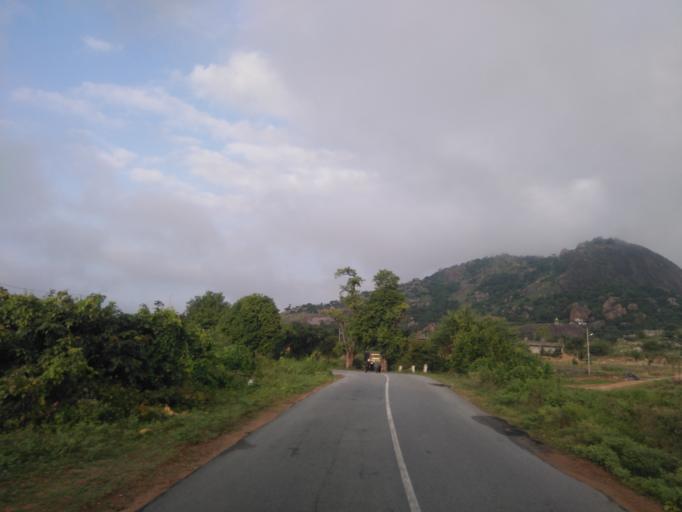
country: IN
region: Karnataka
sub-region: Ramanagara
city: Kanakapura
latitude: 12.4992
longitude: 77.3838
